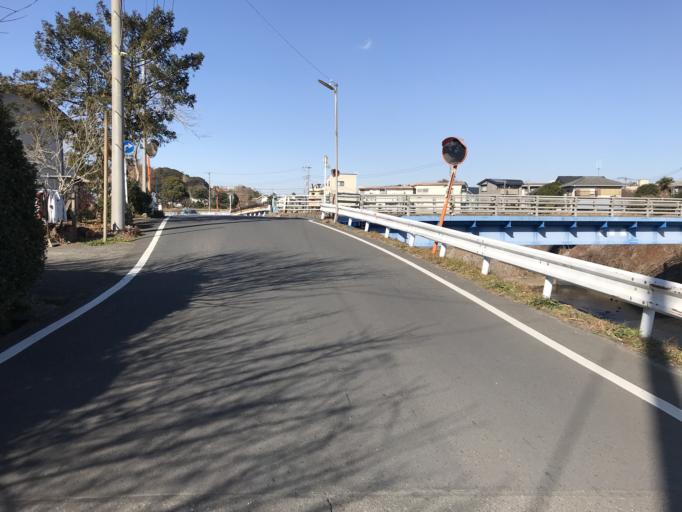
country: JP
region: Tokyo
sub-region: Machida-shi
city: Machida
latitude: 35.5750
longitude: 139.5086
